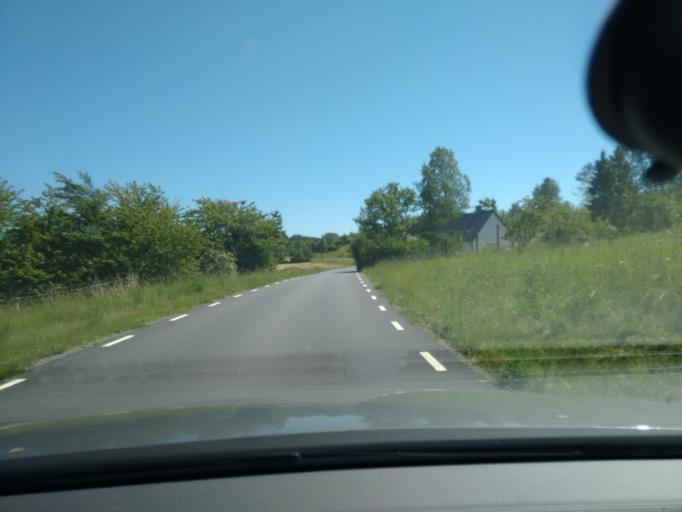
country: SE
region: Skane
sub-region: Kristianstads Kommun
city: Degeberga
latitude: 55.7764
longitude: 14.1142
